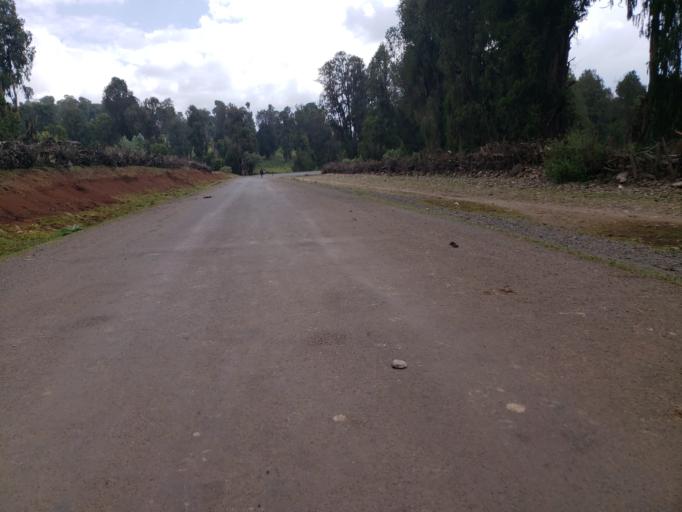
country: ET
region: Oromiya
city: Dodola
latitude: 6.8893
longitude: 39.3898
